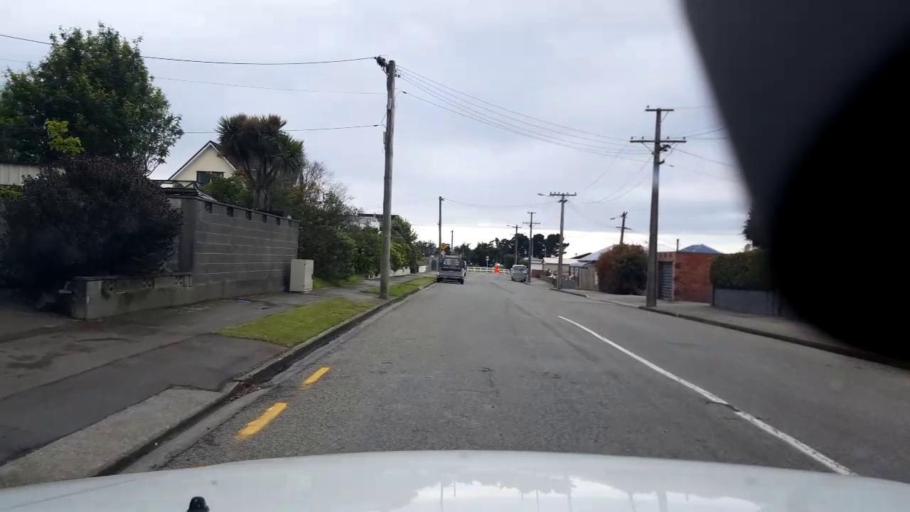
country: NZ
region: Canterbury
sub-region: Timaru District
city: Timaru
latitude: -44.3782
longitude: 171.2420
